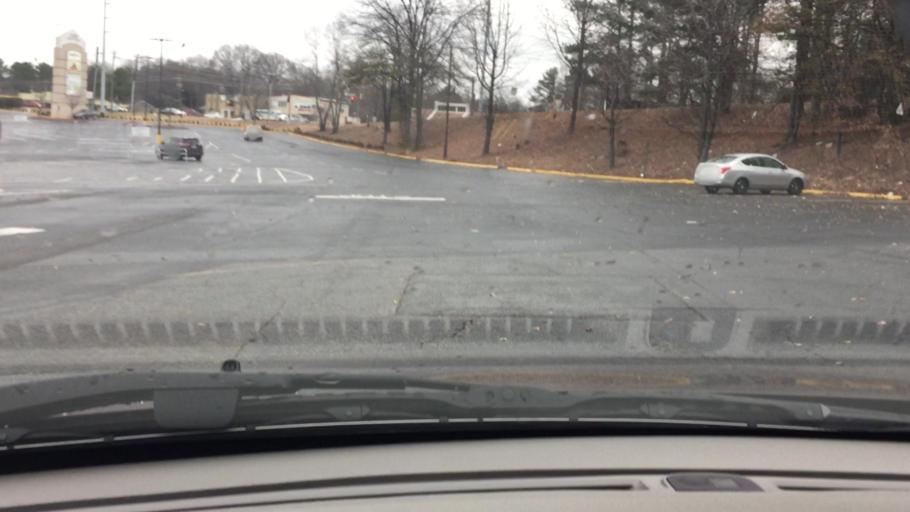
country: US
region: Georgia
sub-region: Cobb County
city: Fair Oaks
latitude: 33.8983
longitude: -84.5419
